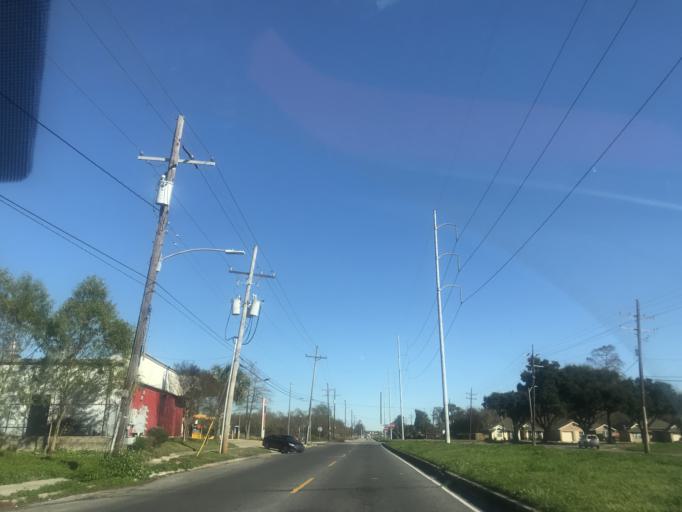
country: US
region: Louisiana
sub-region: Saint Bernard Parish
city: Arabi
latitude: 30.0240
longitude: -89.9899
